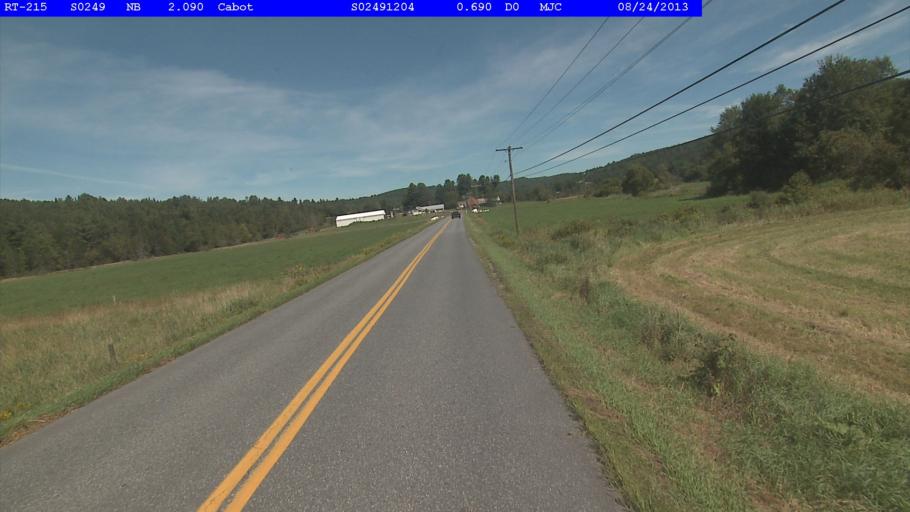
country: US
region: Vermont
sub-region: Caledonia County
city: Hardwick
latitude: 44.3773
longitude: -72.3349
